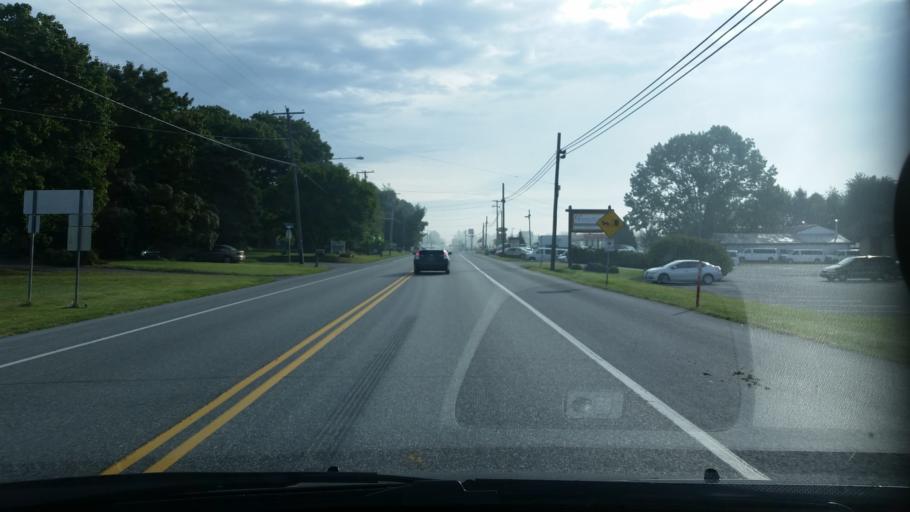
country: US
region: Pennsylvania
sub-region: Lancaster County
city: Brownstown
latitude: 40.0845
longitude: -76.2215
